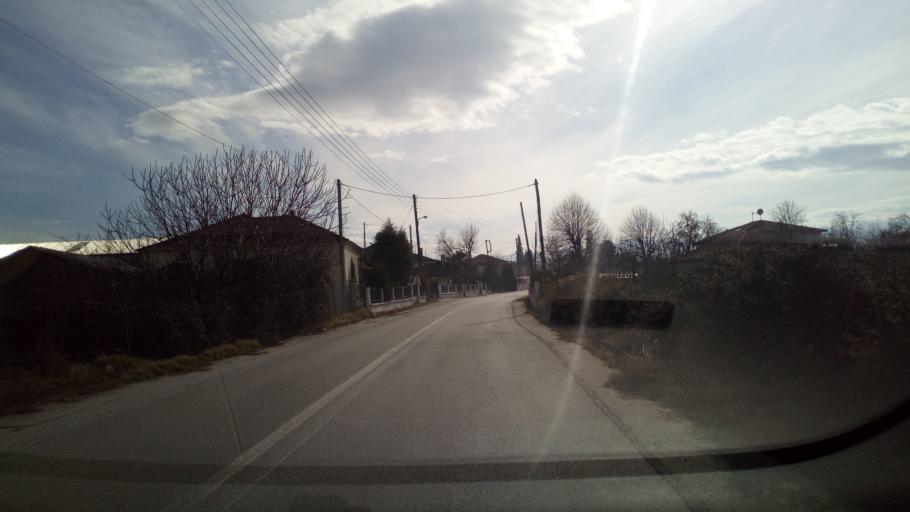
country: GR
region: Central Macedonia
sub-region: Nomos Thessalonikis
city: Gerakarou
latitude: 40.6399
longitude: 23.2464
